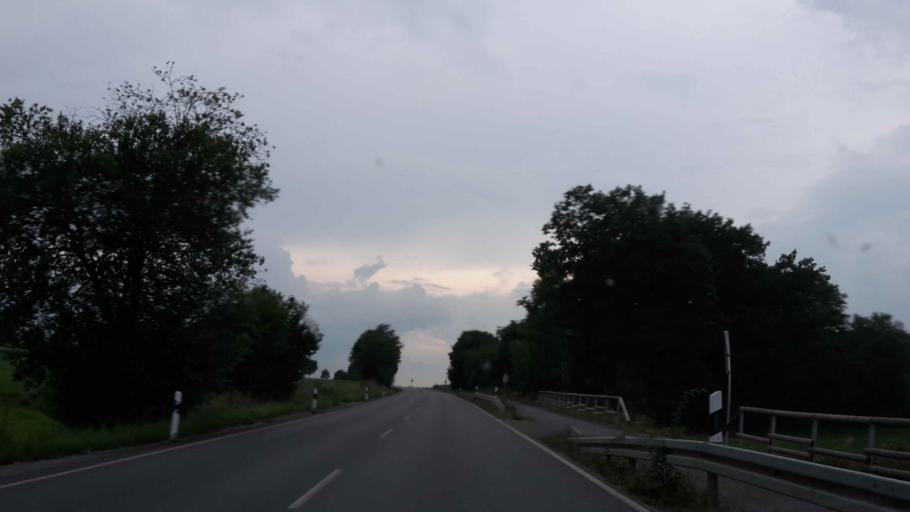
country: DE
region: North Rhine-Westphalia
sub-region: Regierungsbezirk Arnsberg
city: Sundern
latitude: 51.3050
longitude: 7.9729
